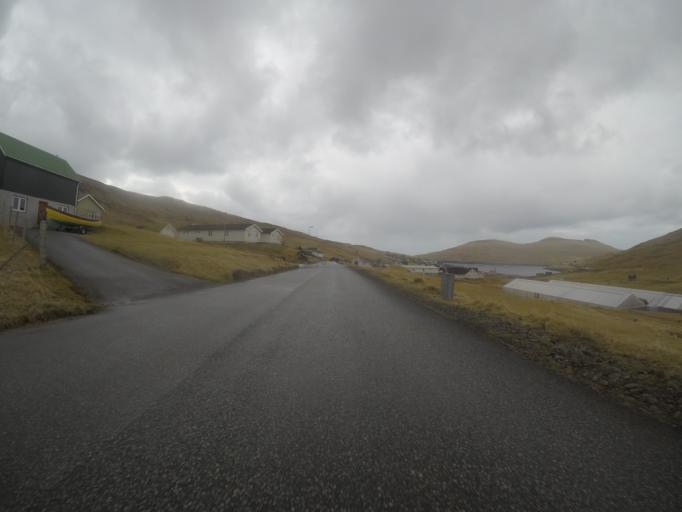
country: FO
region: Vagar
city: Midvagur
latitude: 62.0624
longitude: -7.1457
